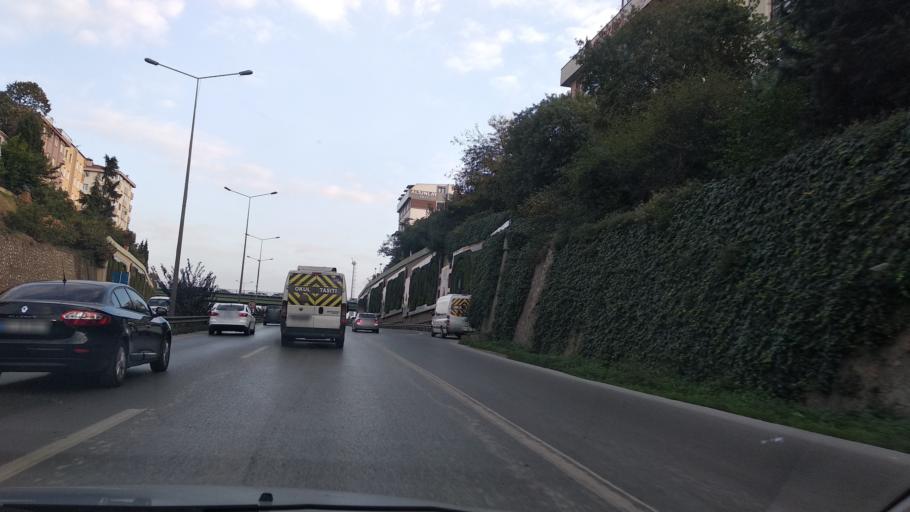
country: TR
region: Istanbul
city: Pendik
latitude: 40.8609
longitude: 29.2792
